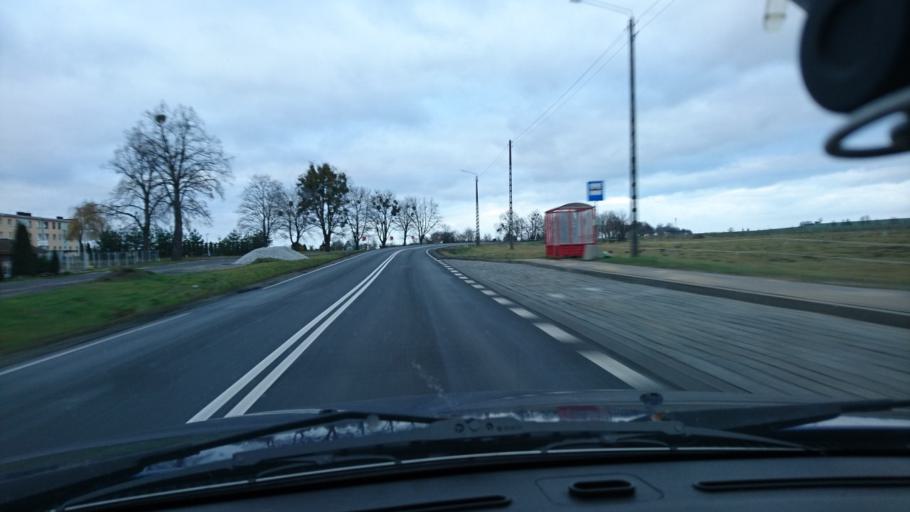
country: PL
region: Opole Voivodeship
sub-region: Powiat kluczborski
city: Byczyna
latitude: 51.0830
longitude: 18.1985
